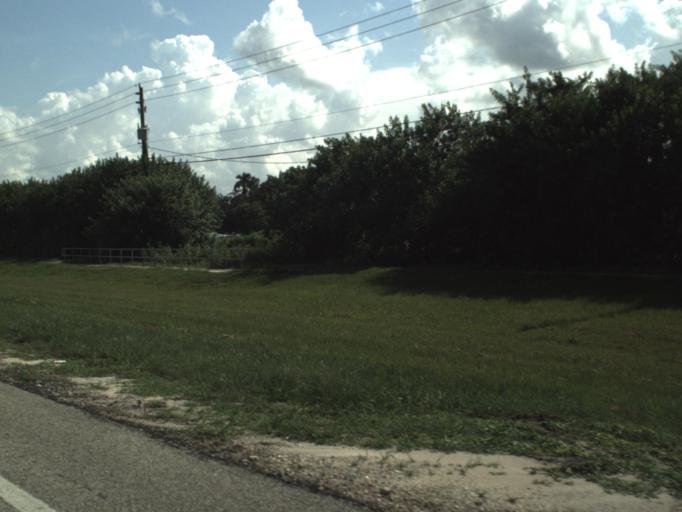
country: US
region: Florida
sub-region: Palm Beach County
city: Villages of Oriole
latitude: 26.5197
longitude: -80.2055
